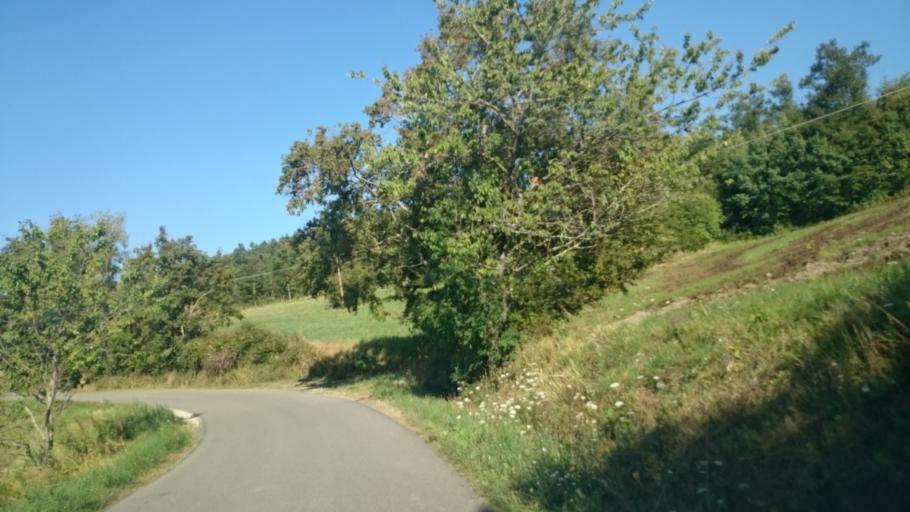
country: IT
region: Emilia-Romagna
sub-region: Provincia di Reggio Emilia
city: Villa Minozzo
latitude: 44.3419
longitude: 10.4799
